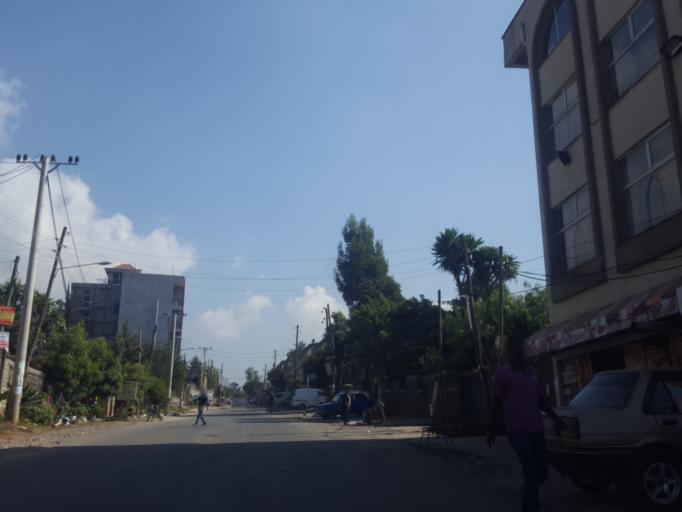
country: ET
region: Adis Abeba
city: Addis Ababa
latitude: 9.0495
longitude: 38.7264
